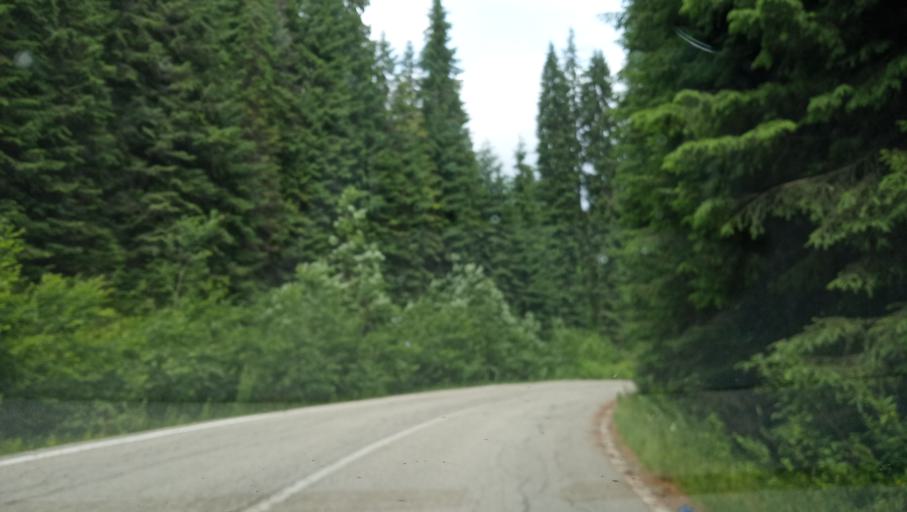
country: RO
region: Valcea
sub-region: Comuna Voineasa
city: Voineasa
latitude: 45.4249
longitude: 23.7470
